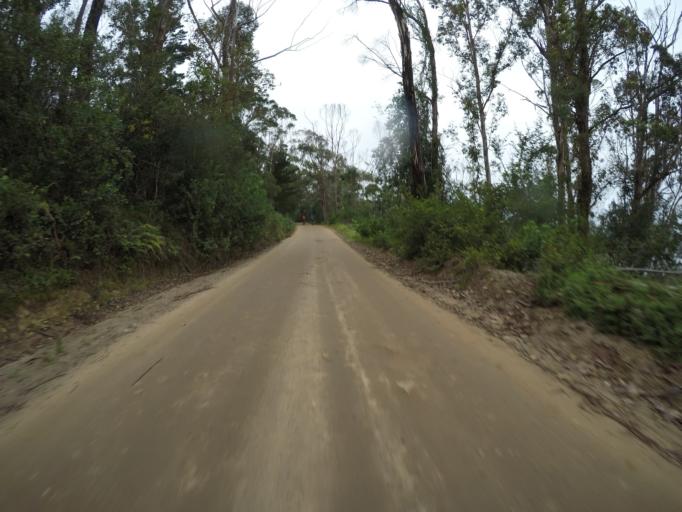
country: ZA
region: Western Cape
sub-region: Eden District Municipality
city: Knysna
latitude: -34.0086
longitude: 22.8004
